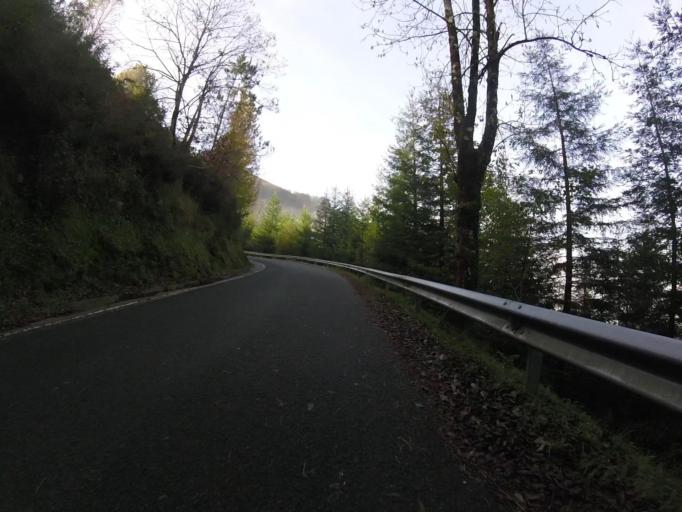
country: ES
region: Navarre
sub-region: Provincia de Navarra
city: Arano
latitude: 43.2042
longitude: -1.8877
